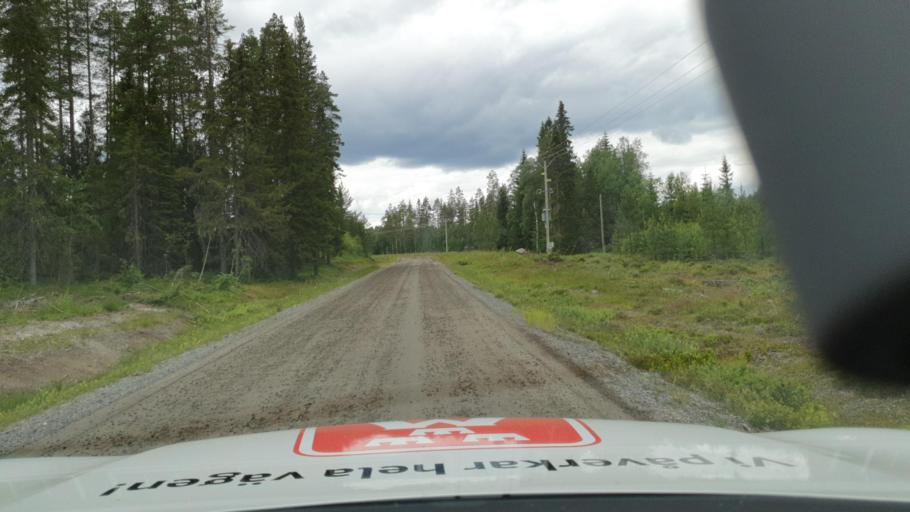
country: SE
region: Vaesterbotten
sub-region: Bjurholms Kommun
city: Bjurholm
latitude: 63.8072
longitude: 19.0747
